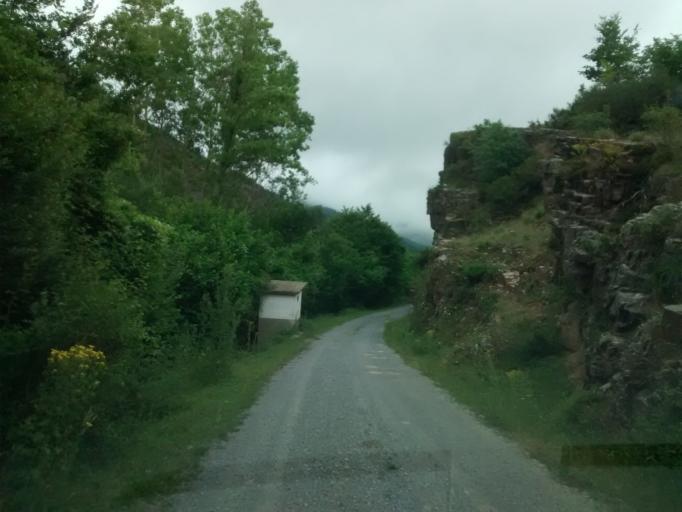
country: ES
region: La Rioja
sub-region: Provincia de La Rioja
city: Ajamil
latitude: 42.1600
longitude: -2.4841
